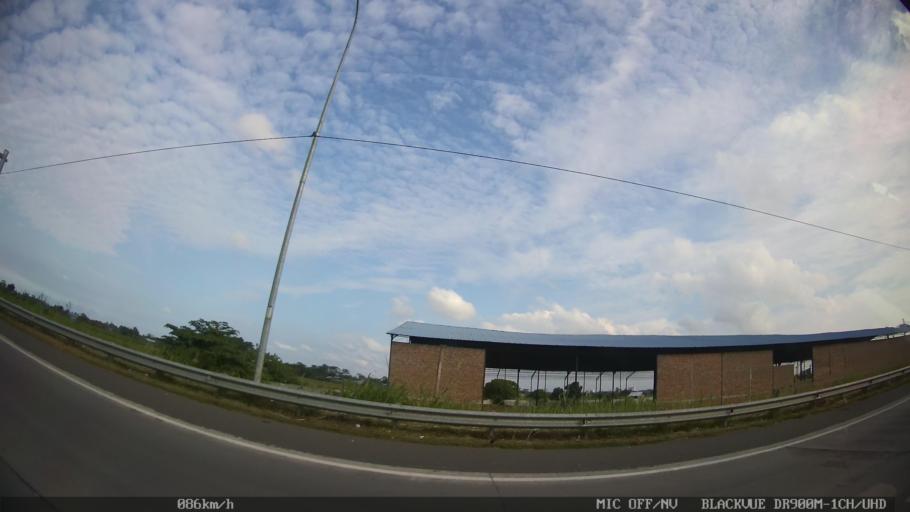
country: ID
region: North Sumatra
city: Medan
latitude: 3.6400
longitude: 98.6452
